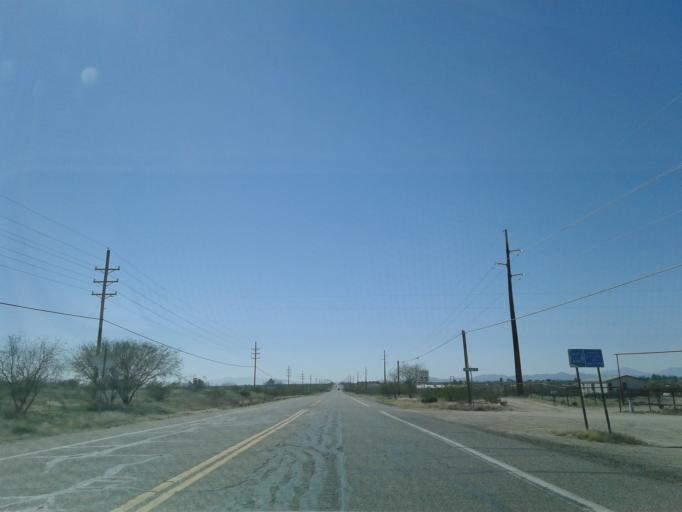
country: US
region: Arizona
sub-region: Pima County
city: Avra Valley
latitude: 32.4432
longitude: -111.3043
